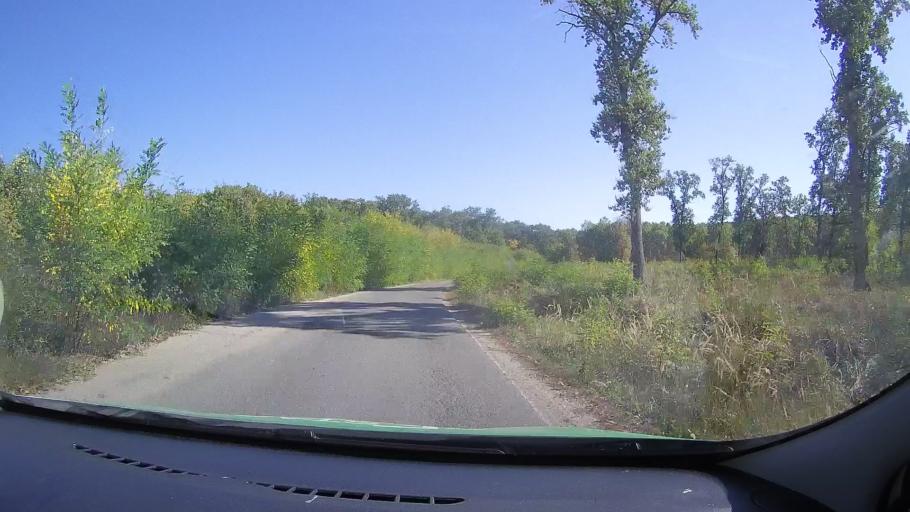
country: RO
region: Satu Mare
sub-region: Comuna Doba
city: Doba
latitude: 47.7173
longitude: 22.7390
